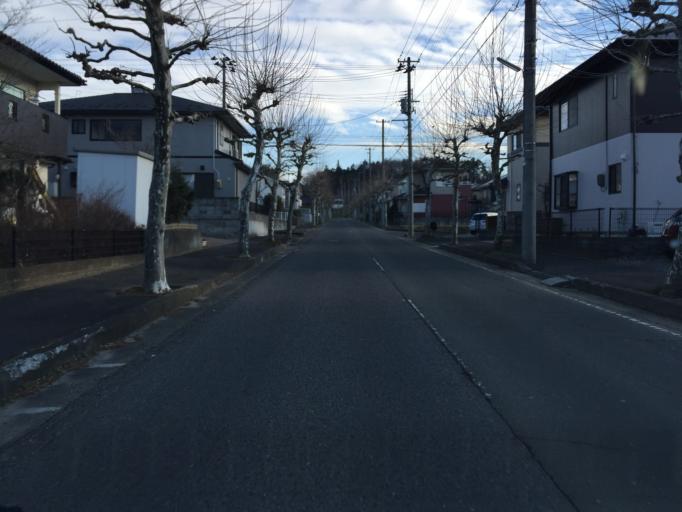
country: JP
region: Fukushima
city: Fukushima-shi
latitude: 37.7194
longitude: 140.4059
